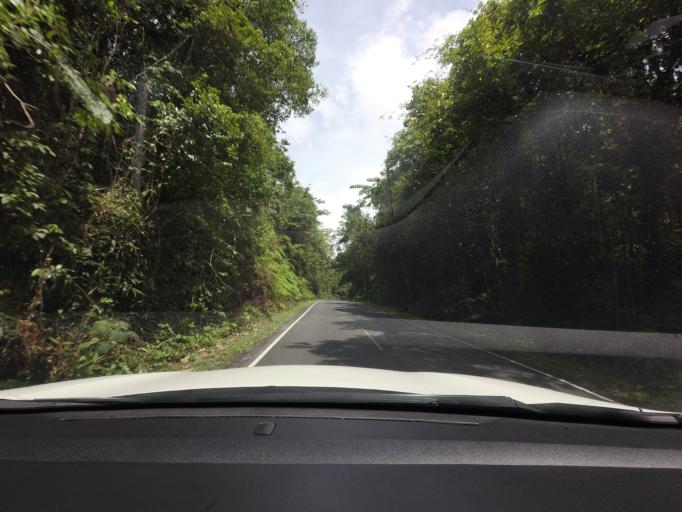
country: TH
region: Nakhon Nayok
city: Pak Phli
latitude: 14.3305
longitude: 101.3587
